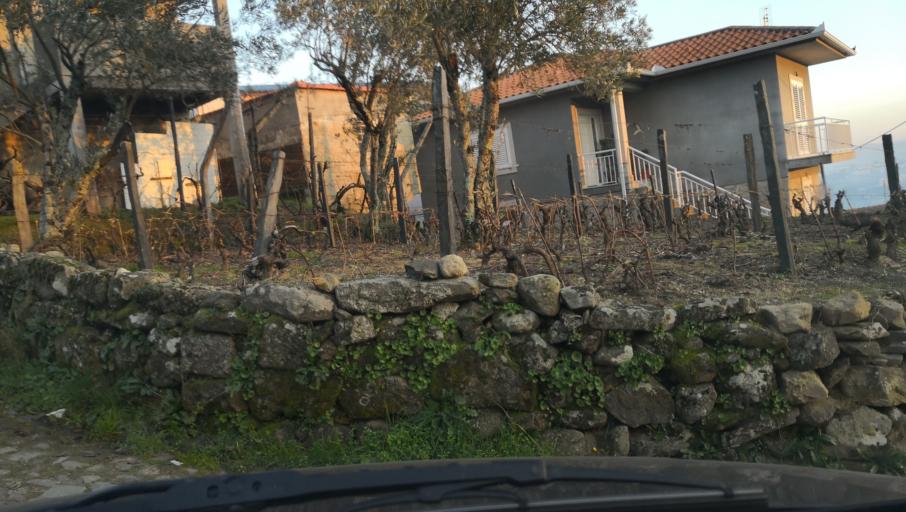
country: PT
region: Vila Real
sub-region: Vila Real
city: Vila Real
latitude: 41.3283
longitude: -7.7524
